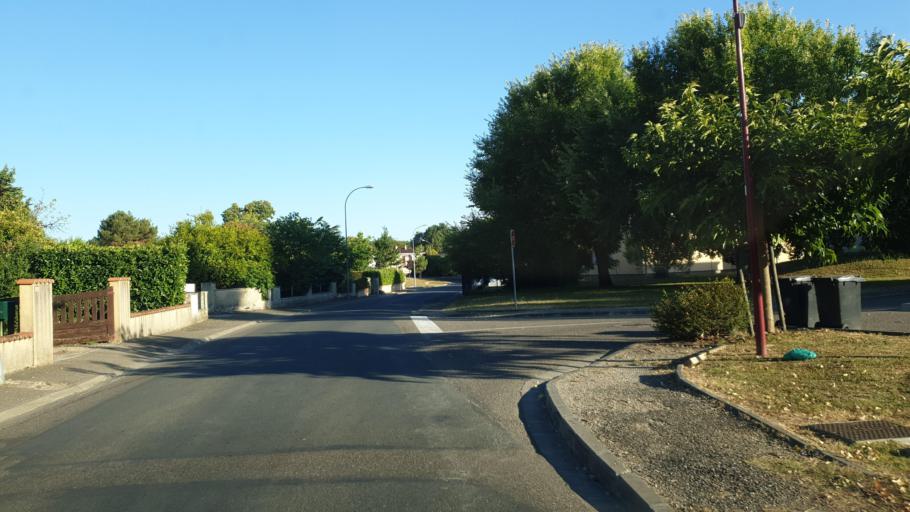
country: FR
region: Aquitaine
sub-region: Departement du Lot-et-Garonne
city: Castelmoron-sur-Lot
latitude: 44.3975
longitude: 0.4980
